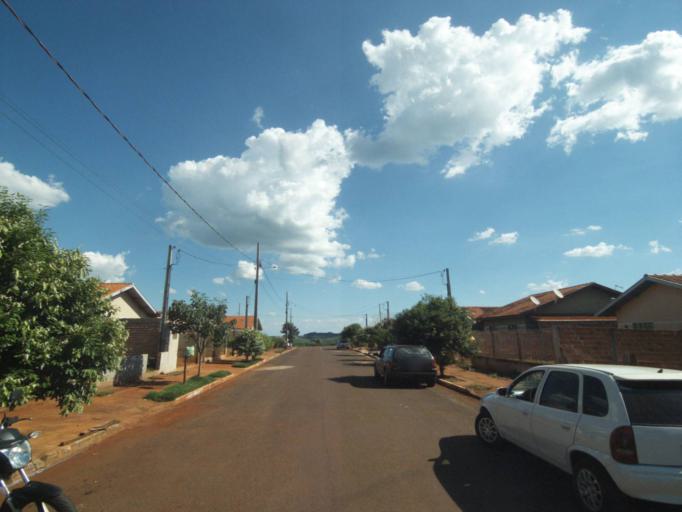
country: BR
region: Parana
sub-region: Sertanopolis
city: Sertanopolis
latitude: -23.0477
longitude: -50.8186
